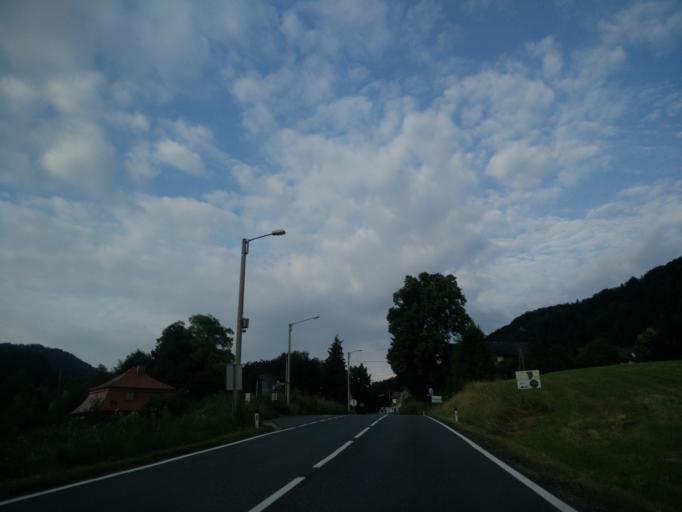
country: AT
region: Salzburg
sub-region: Politischer Bezirk Salzburg-Umgebung
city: Hallwang
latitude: 47.8125
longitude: 13.0830
